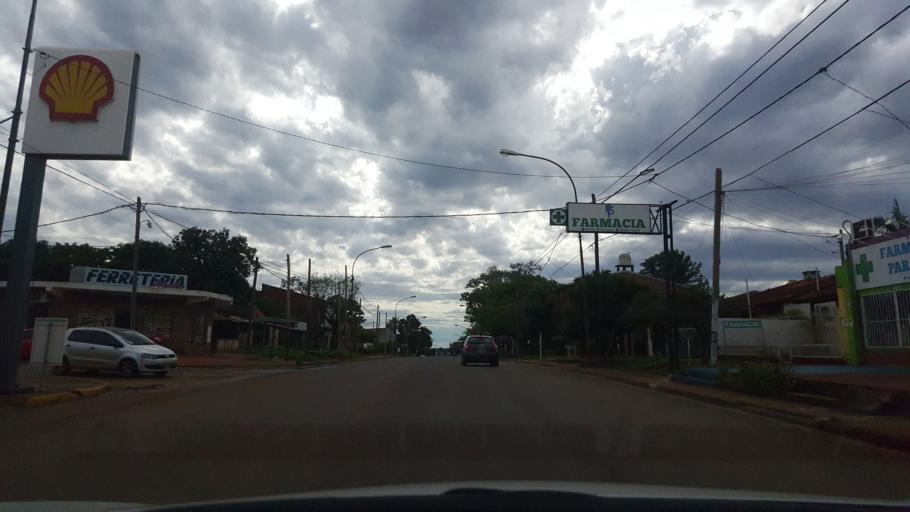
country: AR
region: Misiones
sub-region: Departamento de Capital
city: Posadas
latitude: -27.3713
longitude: -55.9254
